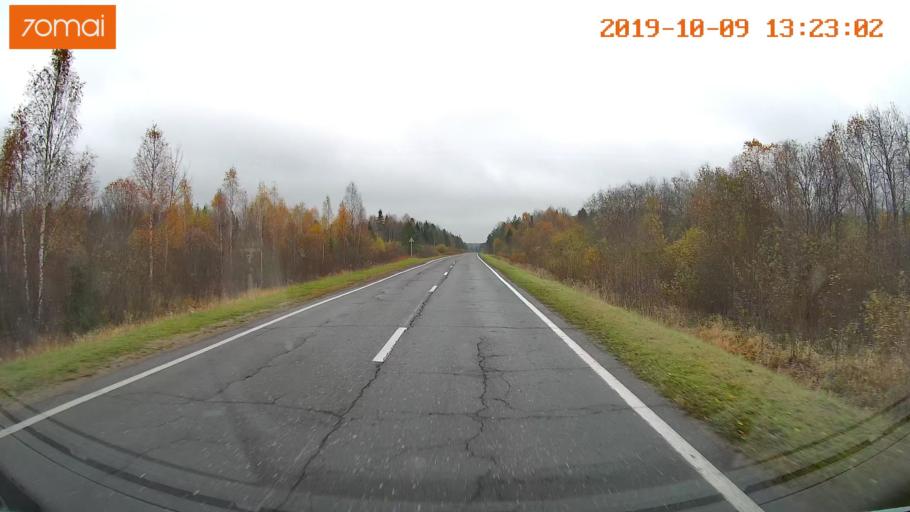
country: RU
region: Jaroslavl
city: Lyubim
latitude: 58.3372
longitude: 40.8790
